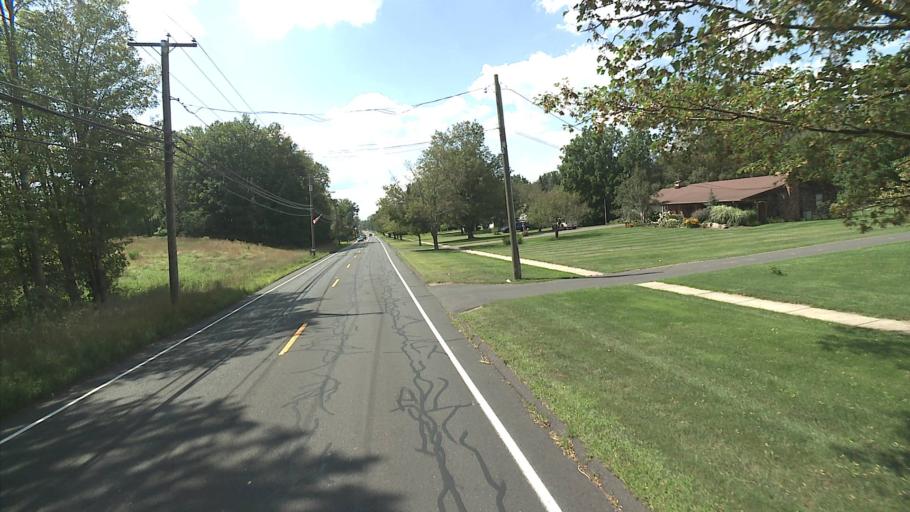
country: US
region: Connecticut
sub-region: Tolland County
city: Somers
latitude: 41.9847
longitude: -72.4345
